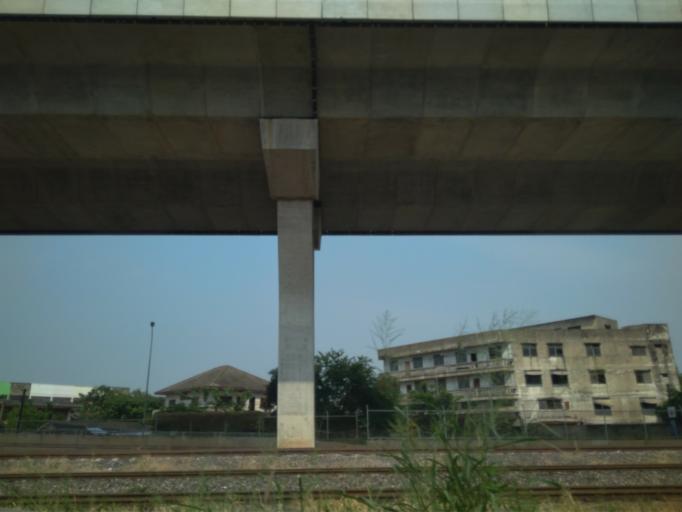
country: TH
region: Bangkok
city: Taling Chan
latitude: 13.7943
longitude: 100.4336
